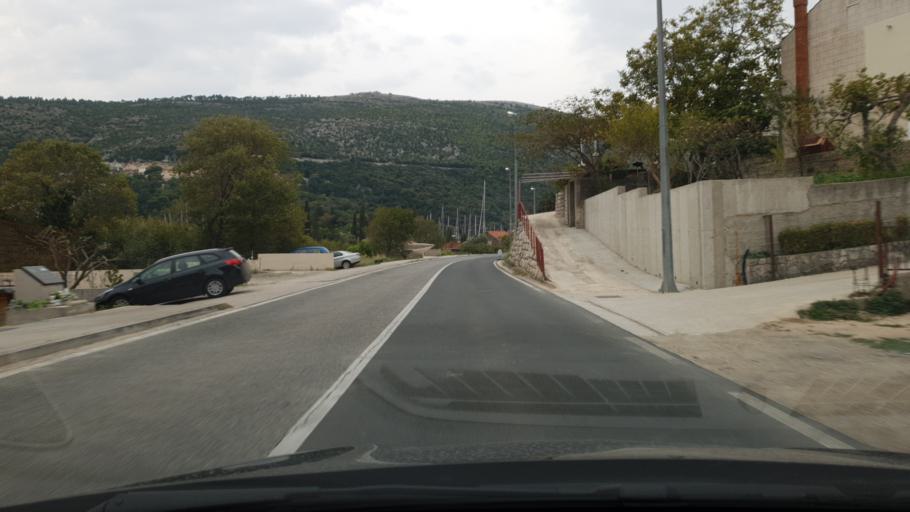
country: HR
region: Dubrovacko-Neretvanska
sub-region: Grad Dubrovnik
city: Mokosica
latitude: 42.6731
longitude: 18.1309
